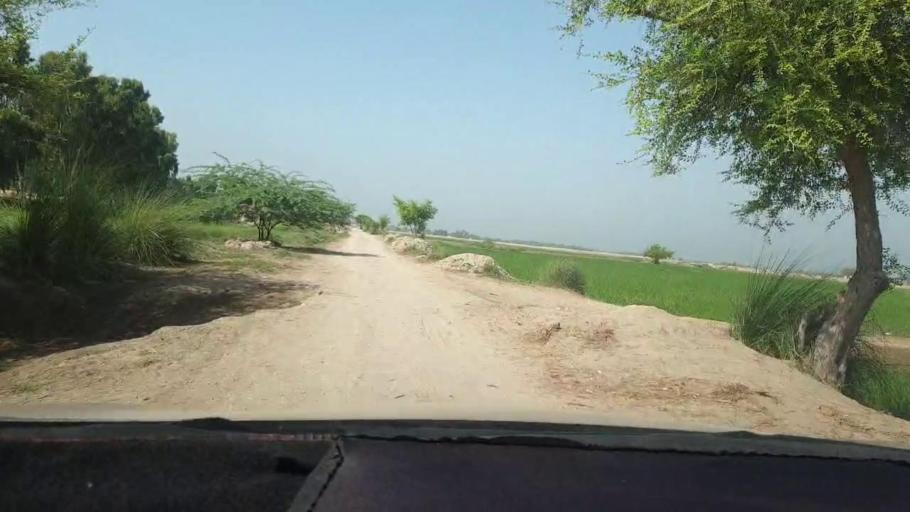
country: PK
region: Sindh
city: Miro Khan
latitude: 27.7147
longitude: 68.1056
